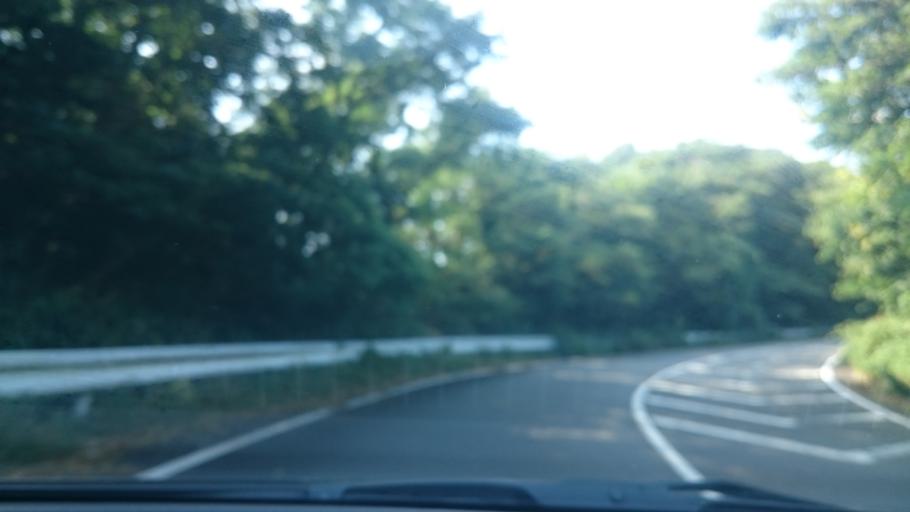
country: JP
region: Shizuoka
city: Heda
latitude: 35.0091
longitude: 138.7802
